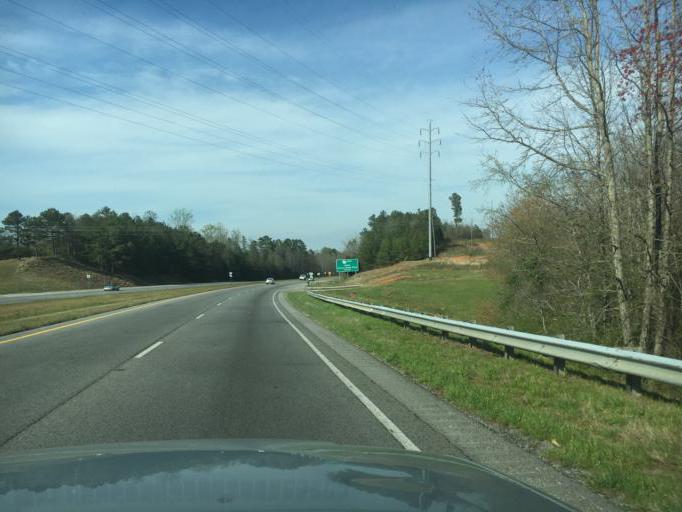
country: US
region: Georgia
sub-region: Banks County
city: Alto
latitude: 34.4922
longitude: -83.5788
